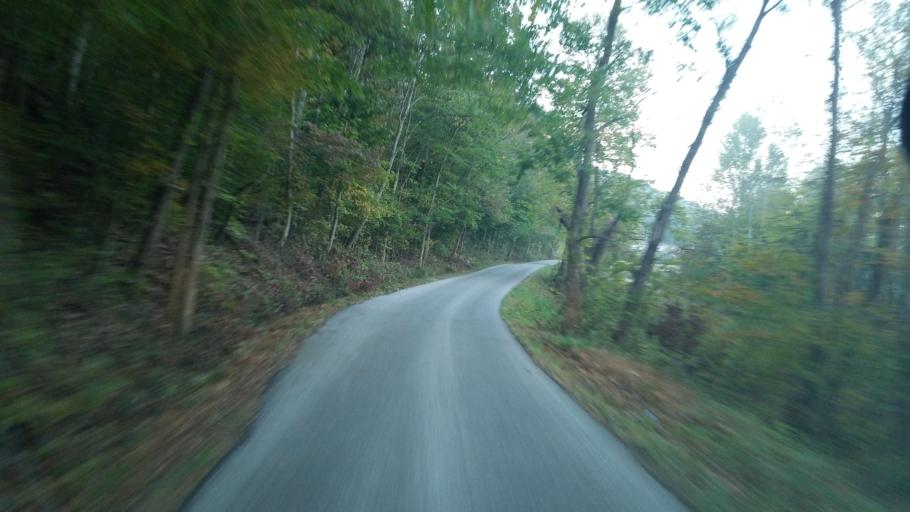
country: US
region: Kentucky
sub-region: Lewis County
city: Vanceburg
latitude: 38.5029
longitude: -83.4838
